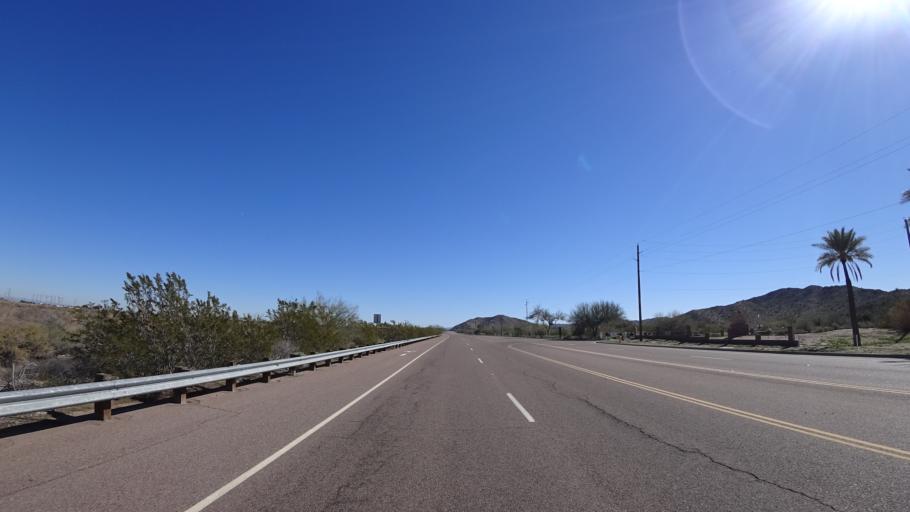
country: US
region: Arizona
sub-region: Maricopa County
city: Goodyear
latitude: 33.3874
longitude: -112.3848
